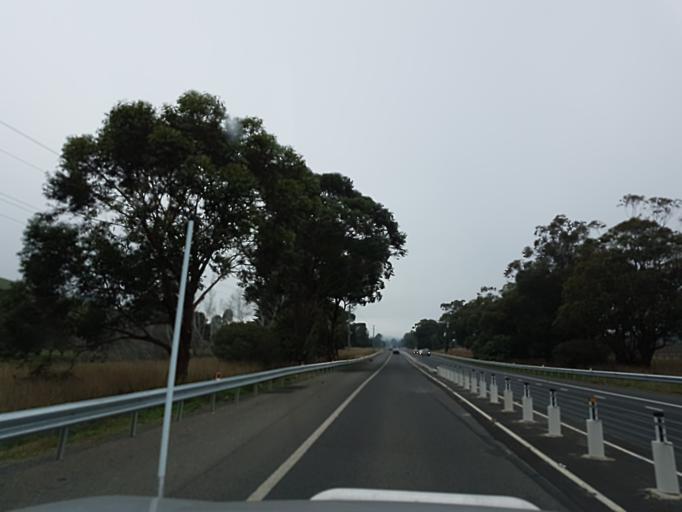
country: AU
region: Victoria
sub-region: Murrindindi
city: Alexandra
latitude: -37.2087
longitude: 145.4560
